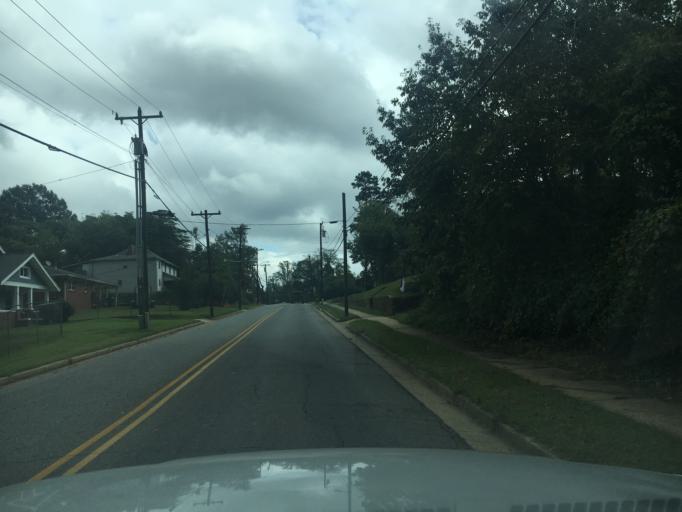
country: US
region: North Carolina
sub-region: Catawba County
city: Hickory
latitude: 35.7288
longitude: -81.3276
